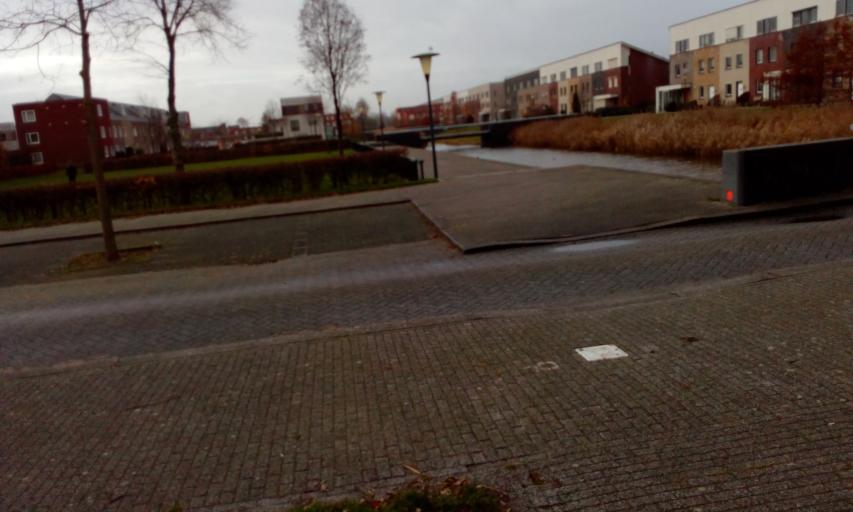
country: NL
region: South Holland
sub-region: Gemeente Rijnwoude
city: Benthuizen
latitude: 52.0623
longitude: 4.5354
